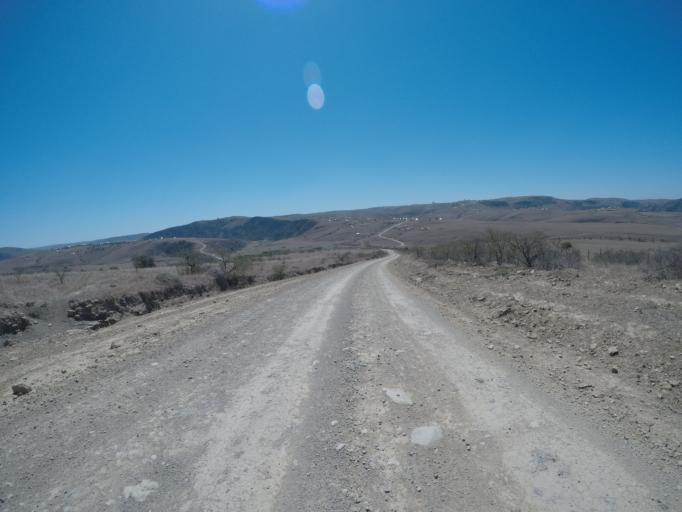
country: ZA
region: Eastern Cape
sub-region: OR Tambo District Municipality
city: Mthatha
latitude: -31.8752
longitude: 28.8725
